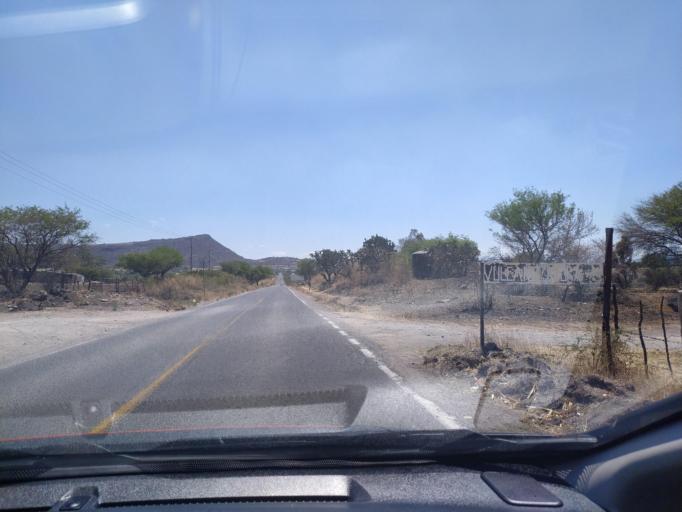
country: MX
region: Guanajuato
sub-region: San Francisco del Rincon
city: San Ignacio de Hidalgo
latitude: 20.8230
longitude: -101.8420
